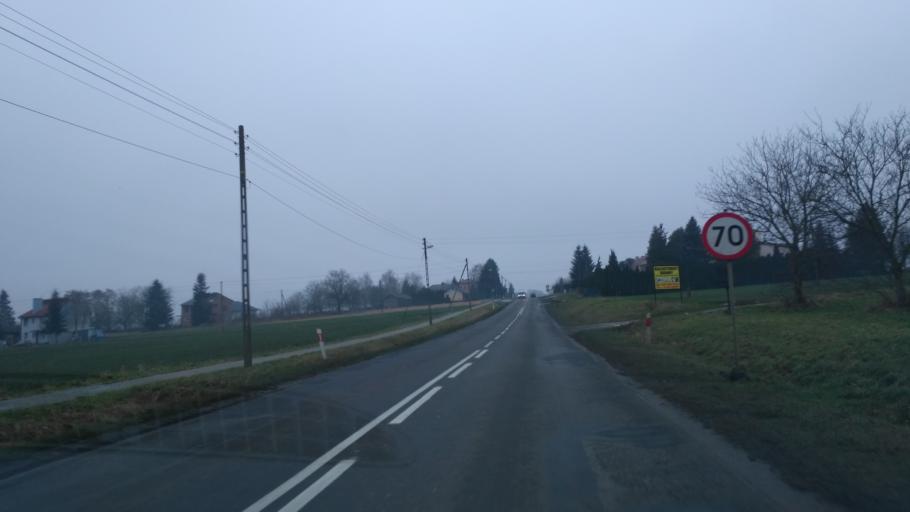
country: PL
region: Subcarpathian Voivodeship
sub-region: Powiat przeworski
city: Urzejowice
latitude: 50.0104
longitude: 22.4535
